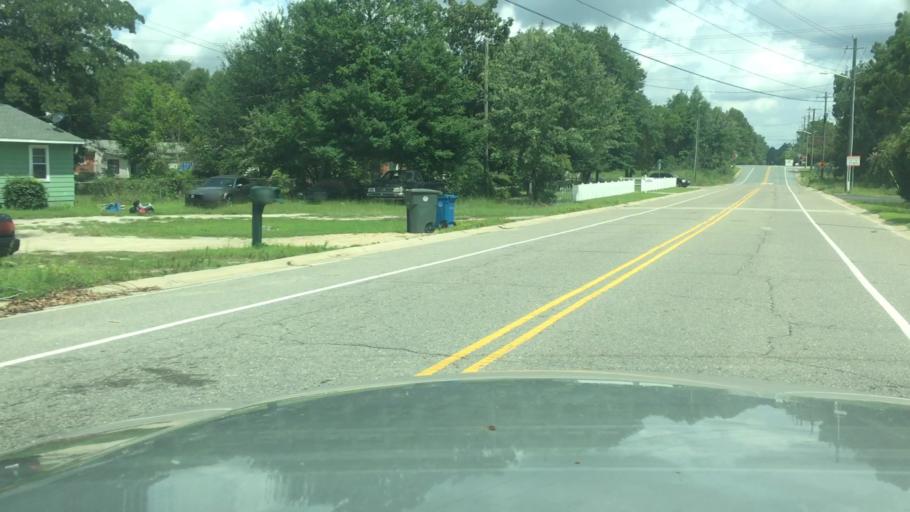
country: US
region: North Carolina
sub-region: Cumberland County
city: Hope Mills
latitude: 35.0196
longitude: -78.9353
